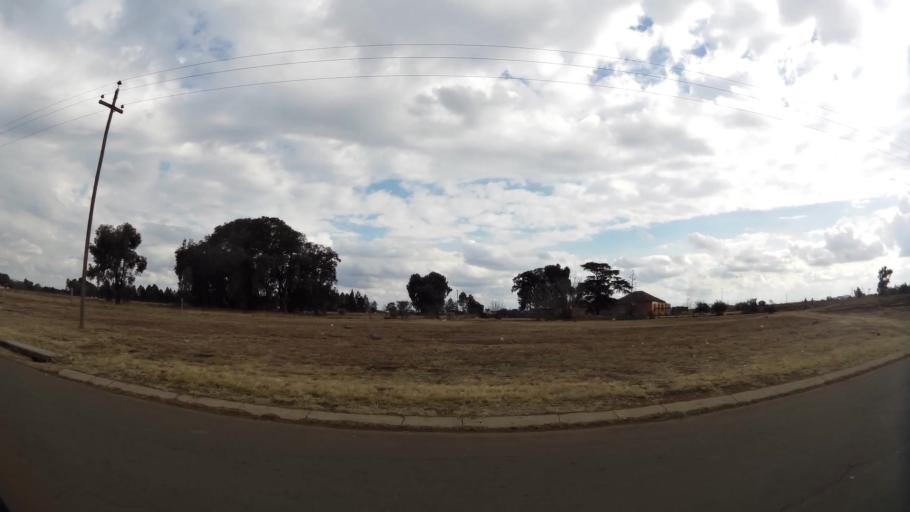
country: ZA
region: Gauteng
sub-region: Sedibeng District Municipality
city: Vanderbijlpark
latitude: -26.7038
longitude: 27.7930
